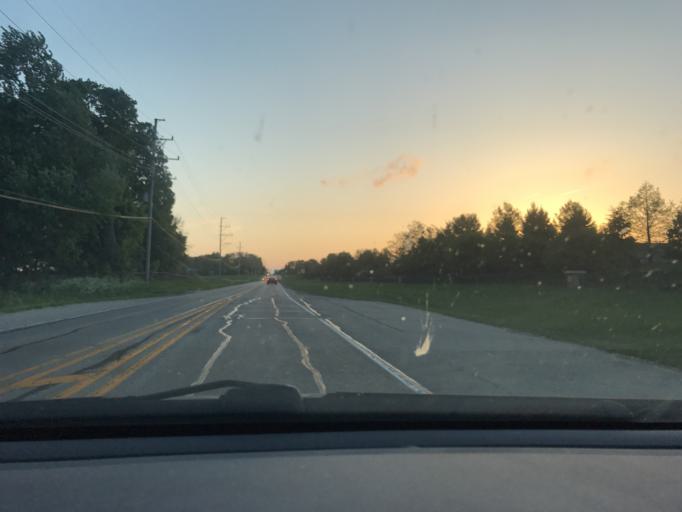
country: US
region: Illinois
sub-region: Kane County
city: South Elgin
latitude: 42.0068
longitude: -88.3520
